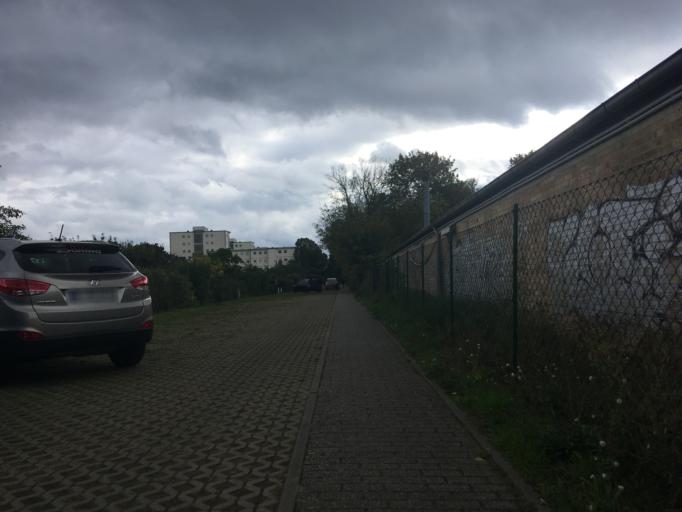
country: DE
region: Berlin
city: Tempelhof Bezirk
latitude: 52.4517
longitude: 13.3964
